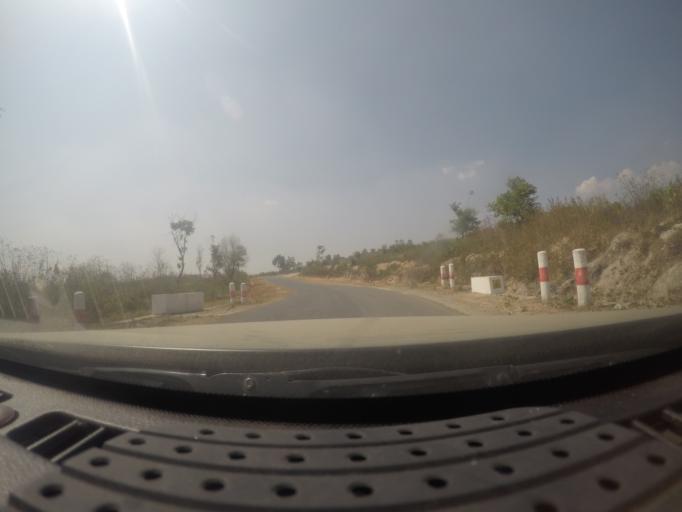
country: MM
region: Shan
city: Taunggyi
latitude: 21.0739
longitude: 96.5010
